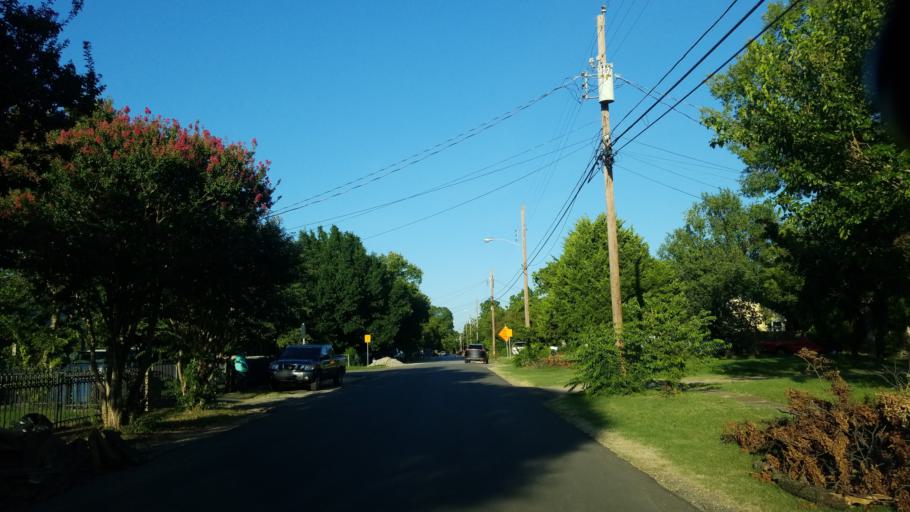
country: US
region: Texas
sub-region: Dallas County
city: Balch Springs
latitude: 32.7770
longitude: -96.6949
